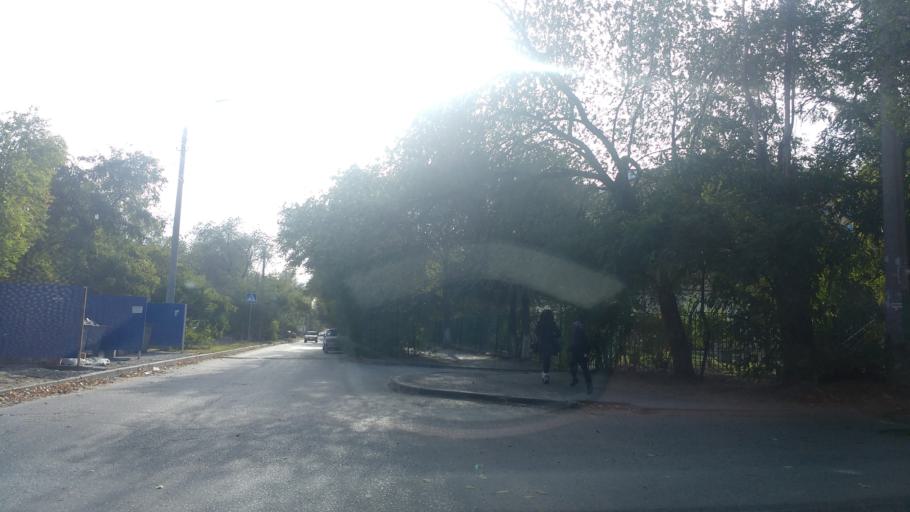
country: RU
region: Volgograd
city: Krasnoslobodsk
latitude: 48.7654
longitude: 44.5578
